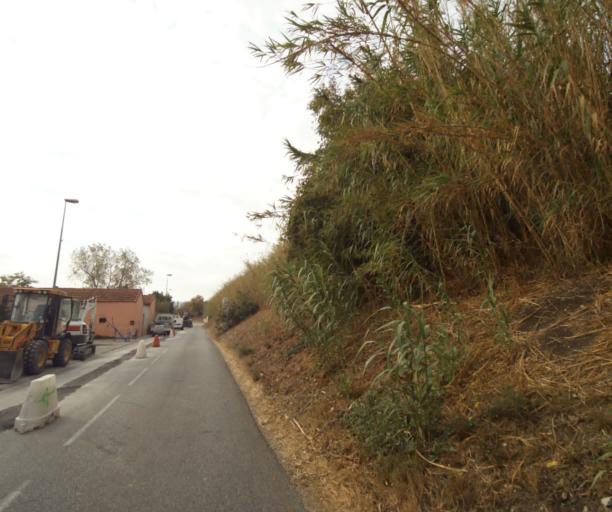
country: FR
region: Provence-Alpes-Cote d'Azur
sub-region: Departement des Bouches-du-Rhone
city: Saint-Victoret
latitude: 43.4146
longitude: 5.2523
